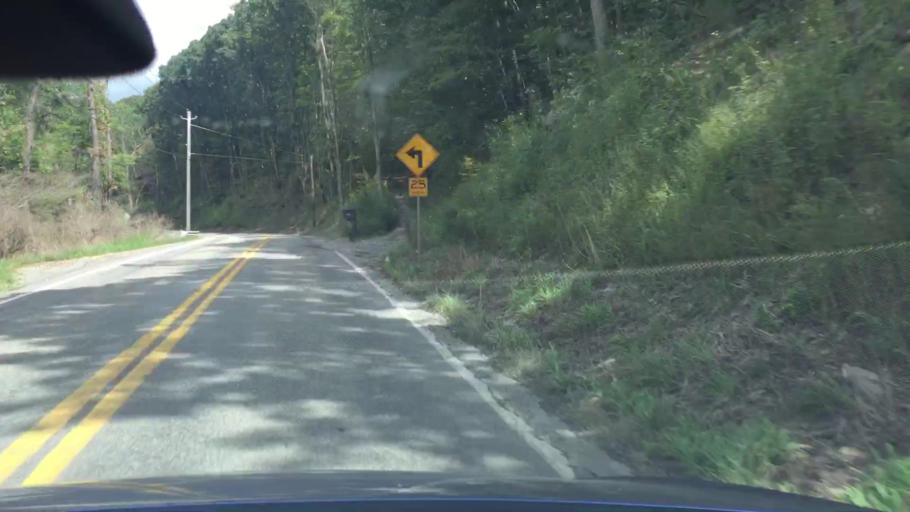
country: US
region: Pennsylvania
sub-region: Allegheny County
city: Curtisville
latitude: 40.6450
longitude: -79.8393
